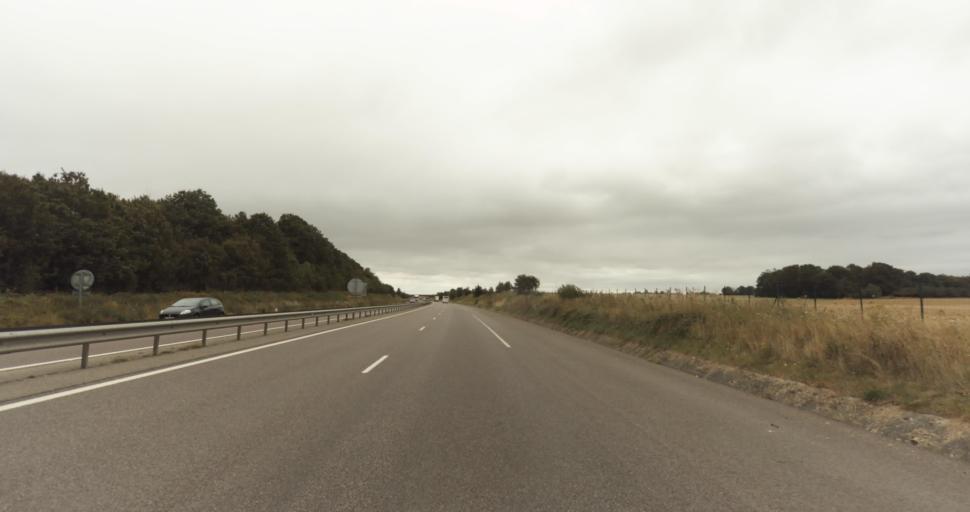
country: FR
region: Haute-Normandie
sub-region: Departement de l'Eure
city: Evreux
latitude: 48.9897
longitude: 1.1946
